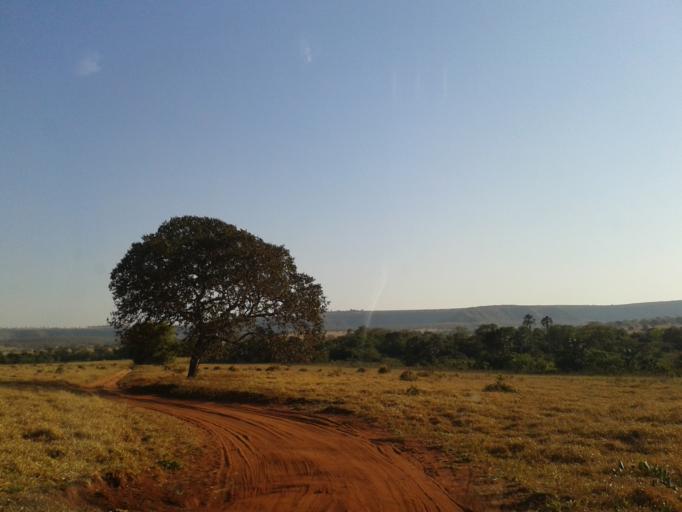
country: BR
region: Minas Gerais
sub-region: Santa Vitoria
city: Santa Vitoria
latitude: -19.1725
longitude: -50.0214
